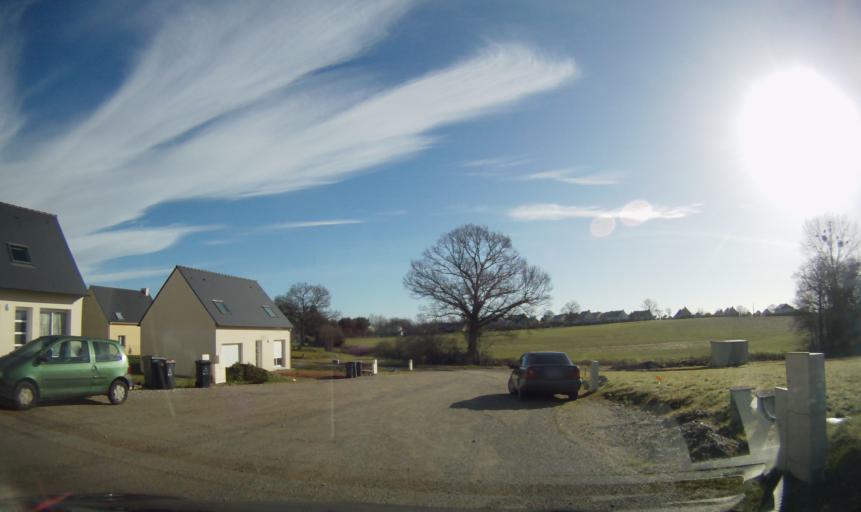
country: FR
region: Brittany
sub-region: Departement d'Ille-et-Vilaine
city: Crevin
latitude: 47.9349
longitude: -1.6534
